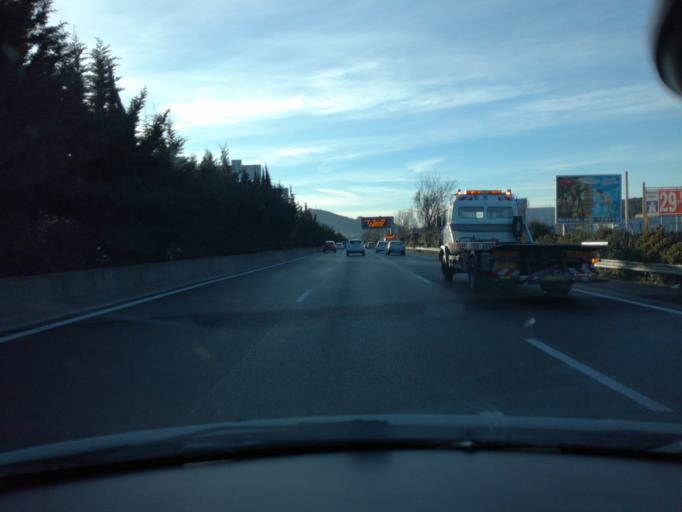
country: FR
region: Provence-Alpes-Cote d'Azur
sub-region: Departement des Bouches-du-Rhone
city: La Penne-sur-Huveaune
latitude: 43.2867
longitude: 5.5335
